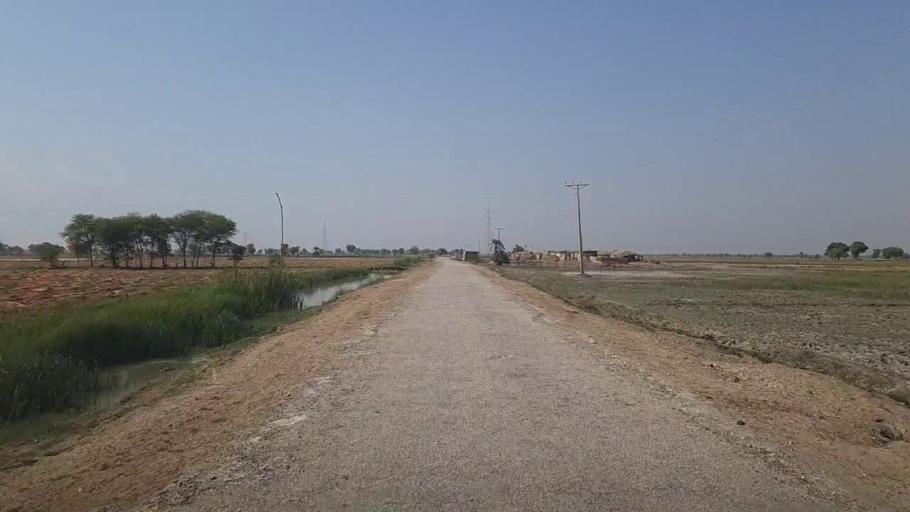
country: PK
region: Sindh
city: Kandhkot
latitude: 28.4082
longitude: 69.2494
